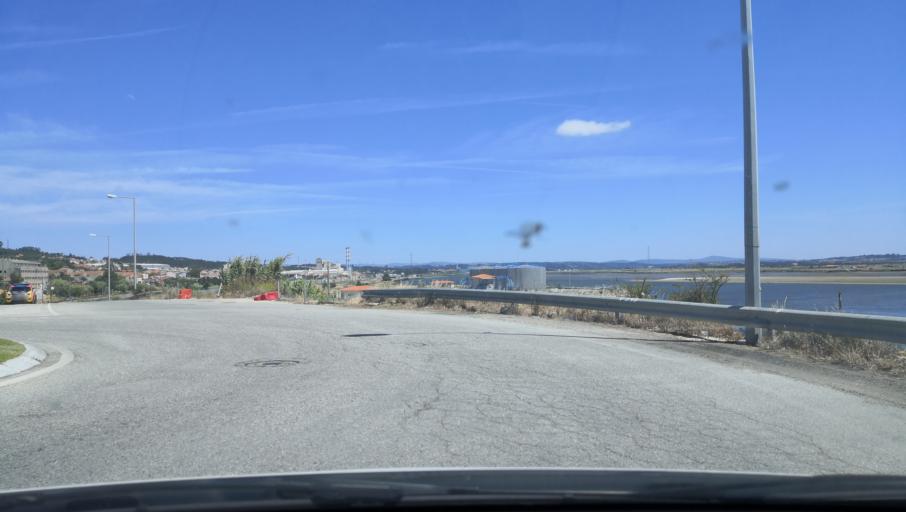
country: PT
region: Coimbra
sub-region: Figueira da Foz
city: Tavarede
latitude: 40.1471
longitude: -8.8329
